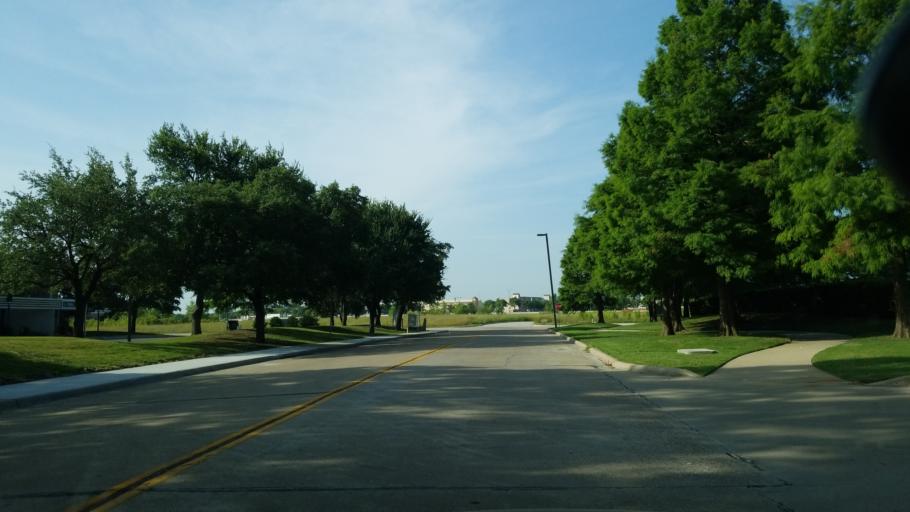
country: US
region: Texas
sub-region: Dallas County
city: Coppell
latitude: 32.9216
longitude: -97.0130
